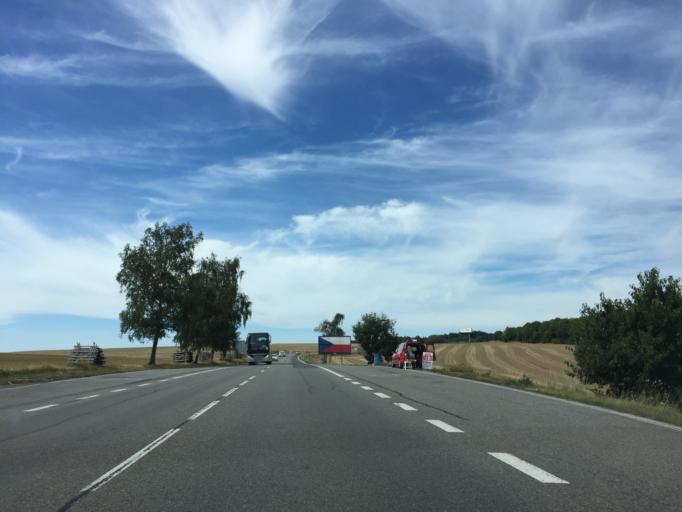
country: CZ
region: Jihocesky
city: Chotoviny
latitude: 49.5571
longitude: 14.6646
